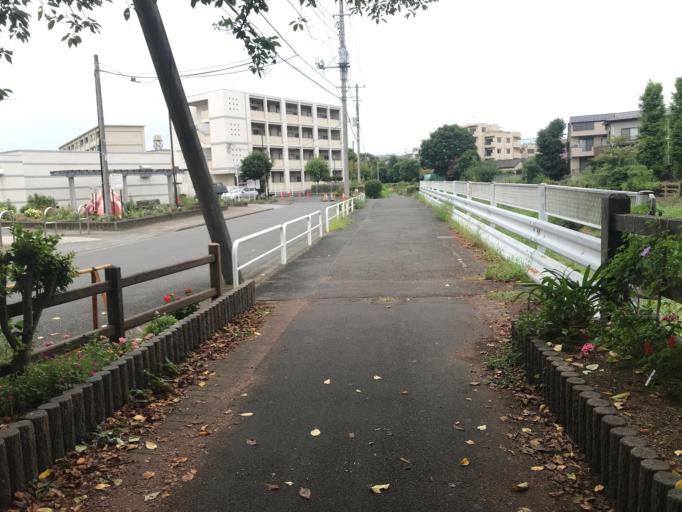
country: JP
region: Tokyo
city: Tanashicho
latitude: 35.7650
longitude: 139.5414
